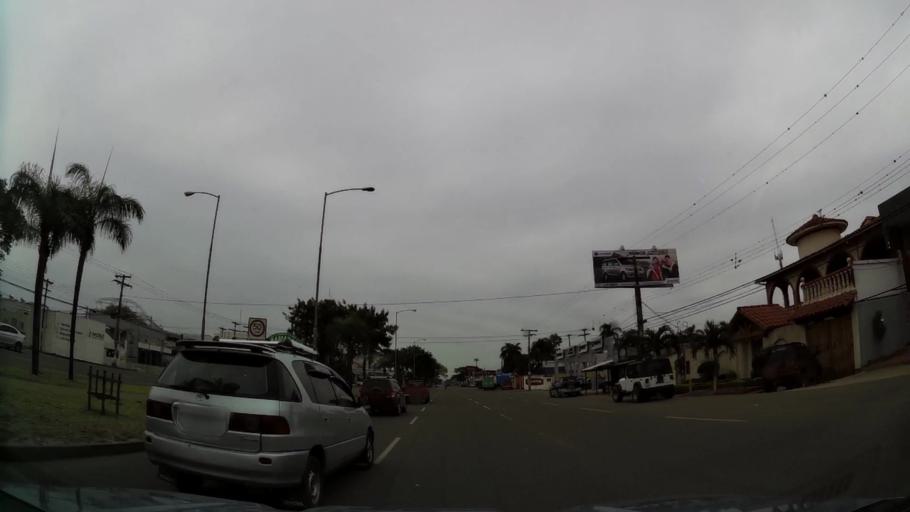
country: BO
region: Santa Cruz
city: Santa Cruz de la Sierra
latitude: -17.8110
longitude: -63.2072
